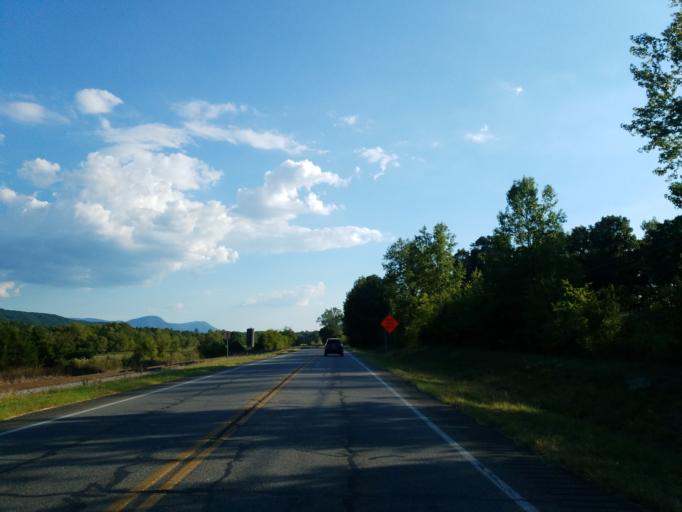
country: US
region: Georgia
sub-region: Murray County
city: Chatsworth
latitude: 34.9106
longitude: -84.7459
